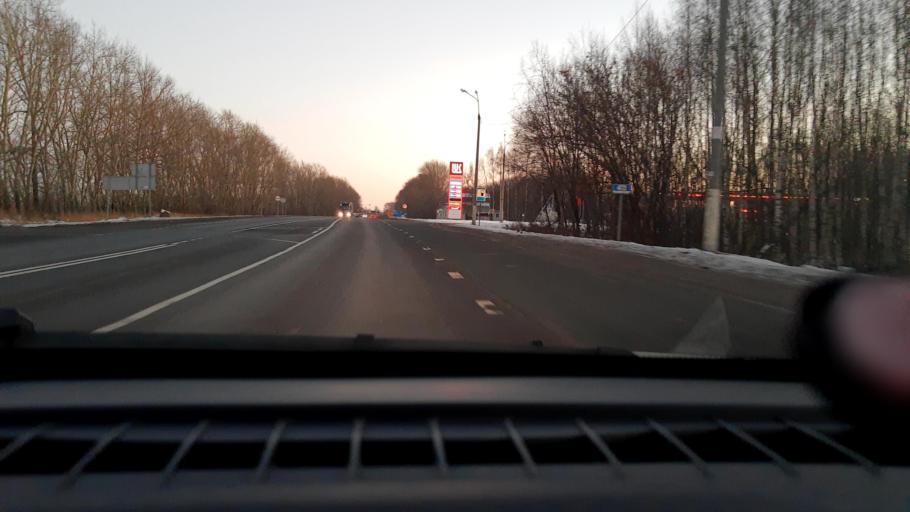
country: RU
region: Nizjnij Novgorod
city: Pamyat' Parizhskoy Kommuny
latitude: 56.0042
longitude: 44.6313
